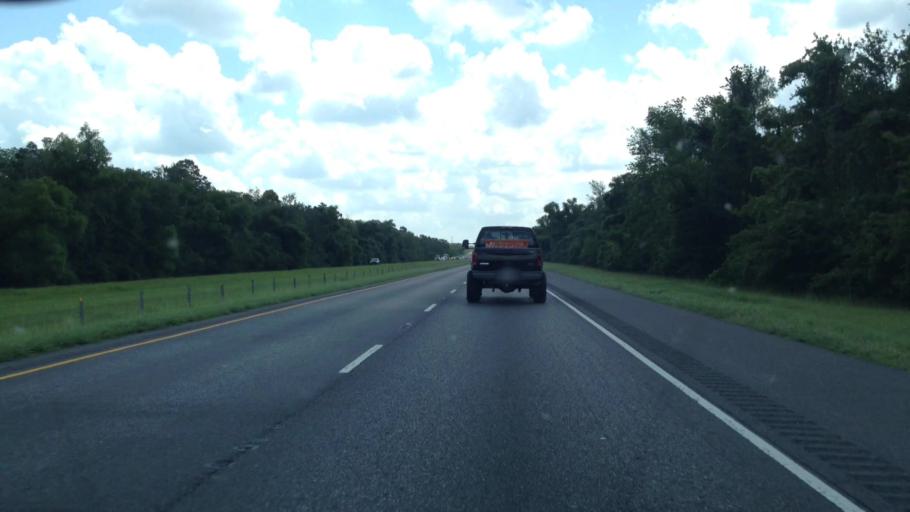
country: US
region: Louisiana
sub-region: Saint James Parish
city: Grand Point
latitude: 30.1340
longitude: -90.7280
